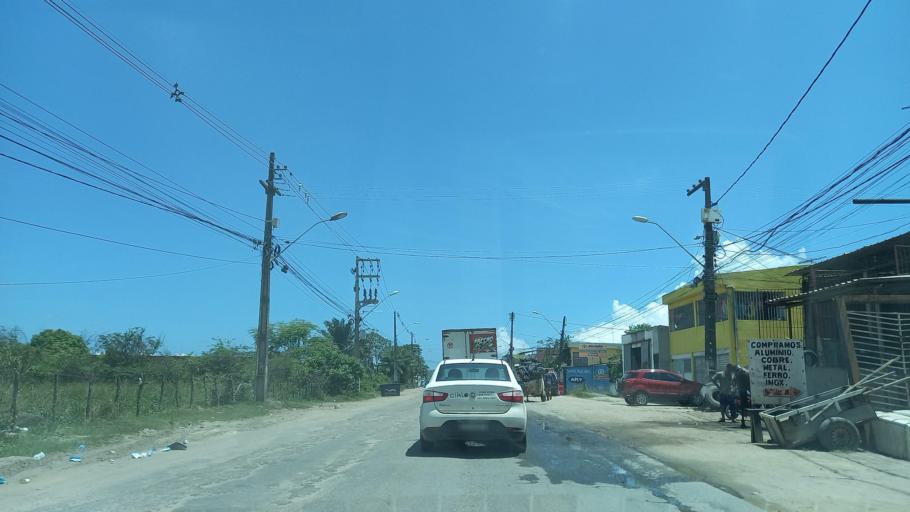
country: BR
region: Pernambuco
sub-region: Jaboatao Dos Guararapes
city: Jaboatao
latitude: -8.1576
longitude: -34.9710
